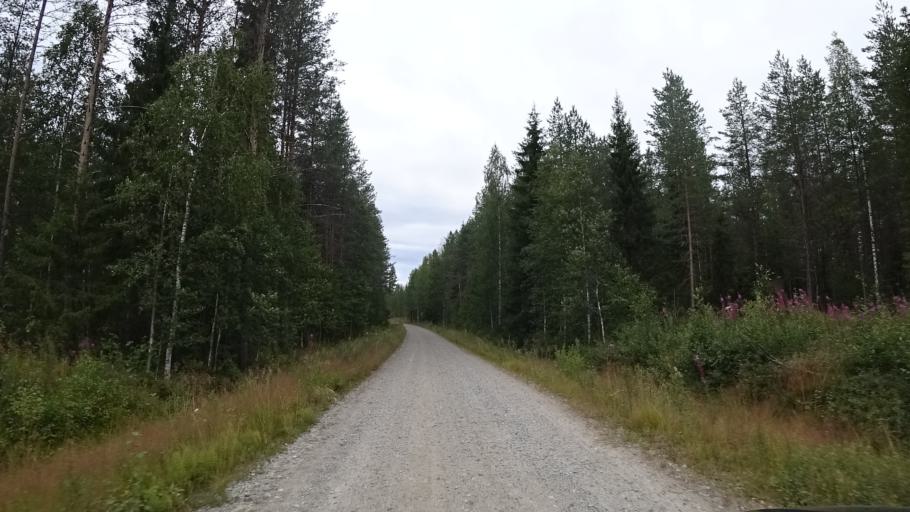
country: FI
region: North Karelia
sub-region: Joensuu
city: Ilomantsi
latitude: 63.1536
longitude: 30.6415
